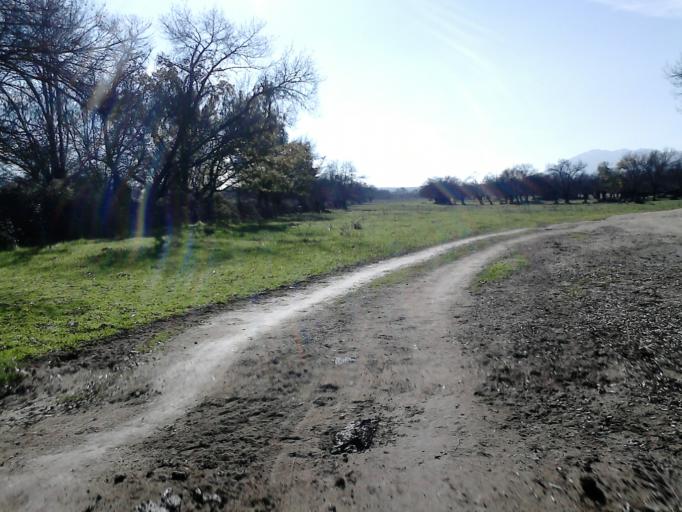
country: ES
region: Madrid
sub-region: Provincia de Madrid
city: El Escorial
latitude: 40.5911
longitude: -4.1141
